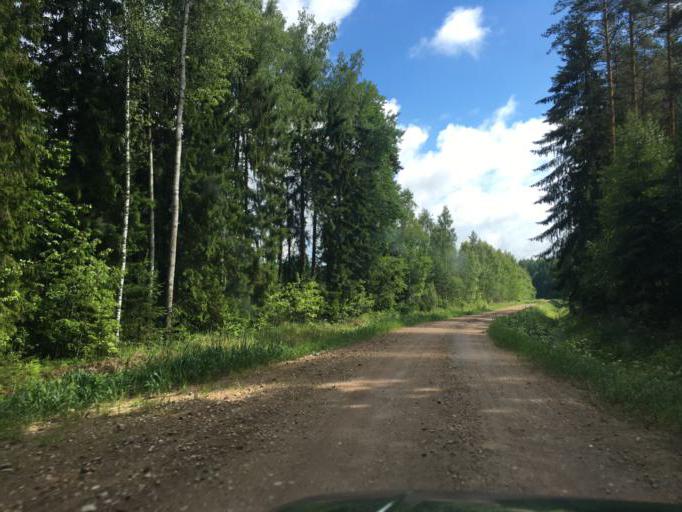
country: LV
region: Balvu Rajons
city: Balvi
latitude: 57.2901
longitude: 27.3158
